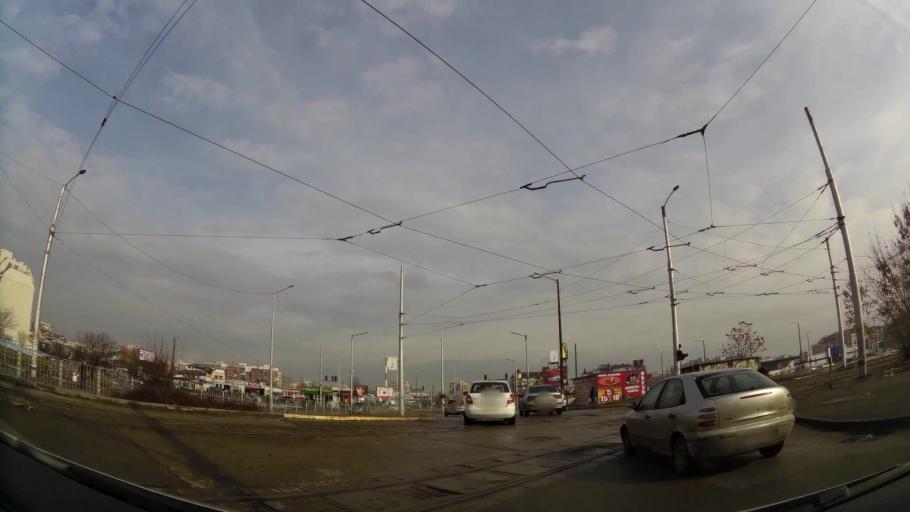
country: BG
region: Sofiya
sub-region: Obshtina Bozhurishte
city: Bozhurishte
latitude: 42.7190
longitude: 23.2542
